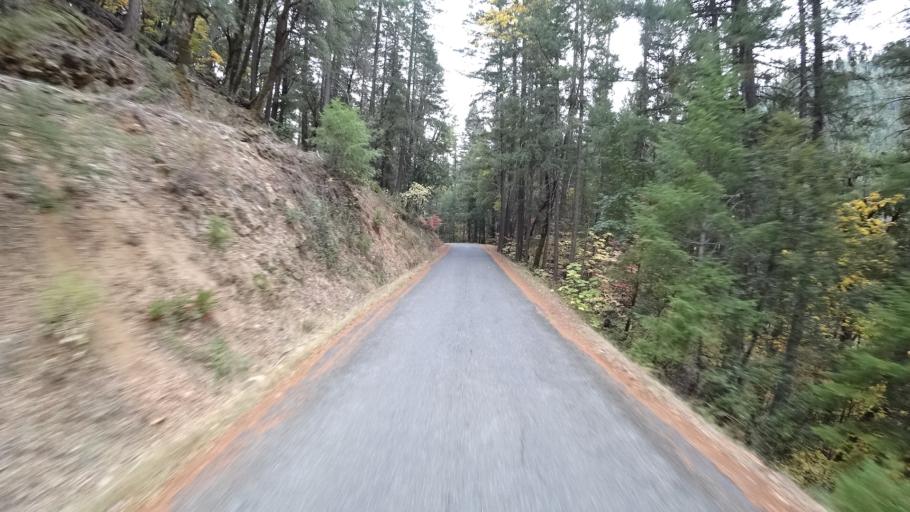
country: US
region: California
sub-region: Siskiyou County
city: Happy Camp
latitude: 41.7528
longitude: -123.3635
